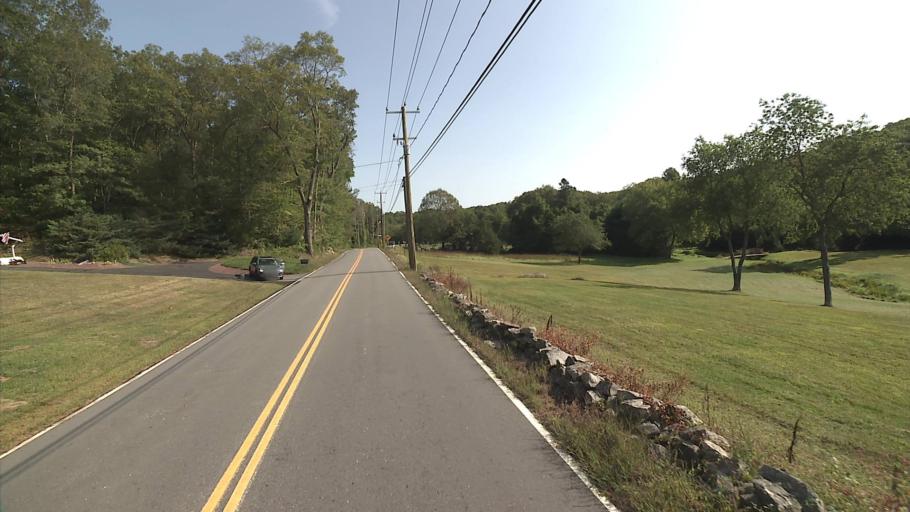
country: US
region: Connecticut
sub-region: New London County
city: Lisbon
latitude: 41.5783
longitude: -72.0288
